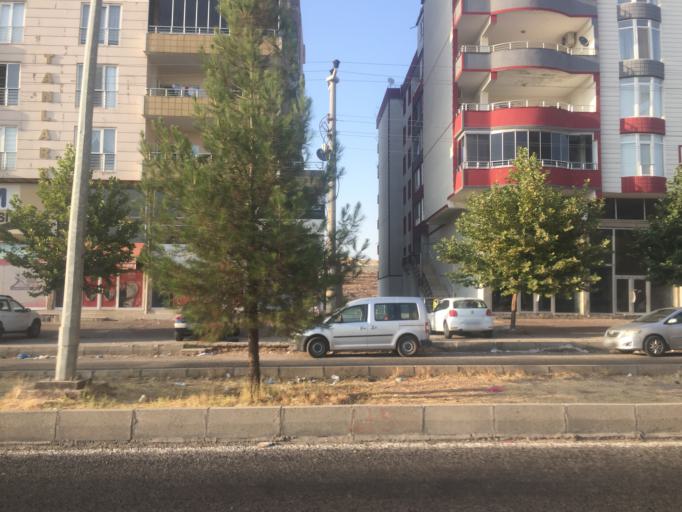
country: TR
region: Mardin
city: Midyat
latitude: 37.4343
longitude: 41.3281
